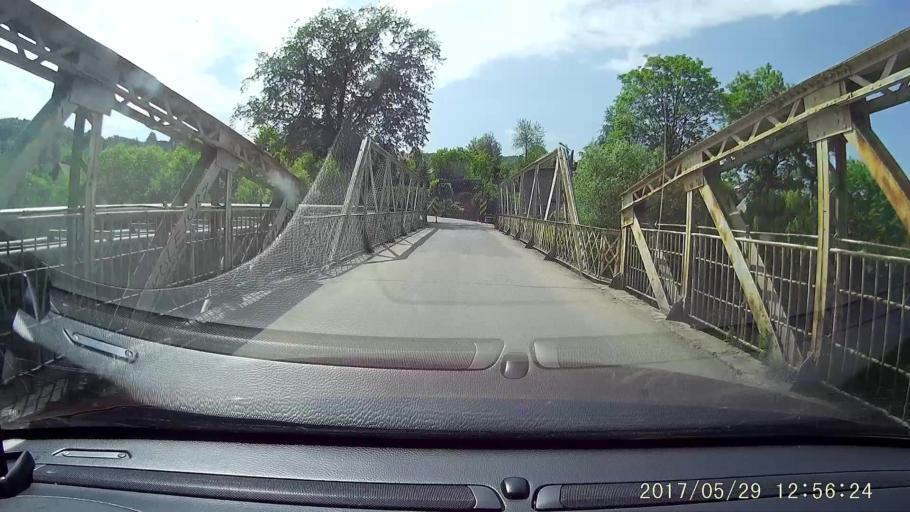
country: PL
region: Lower Silesian Voivodeship
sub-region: Jelenia Gora
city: Jelenia Gora
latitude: 50.9332
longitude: 15.6853
